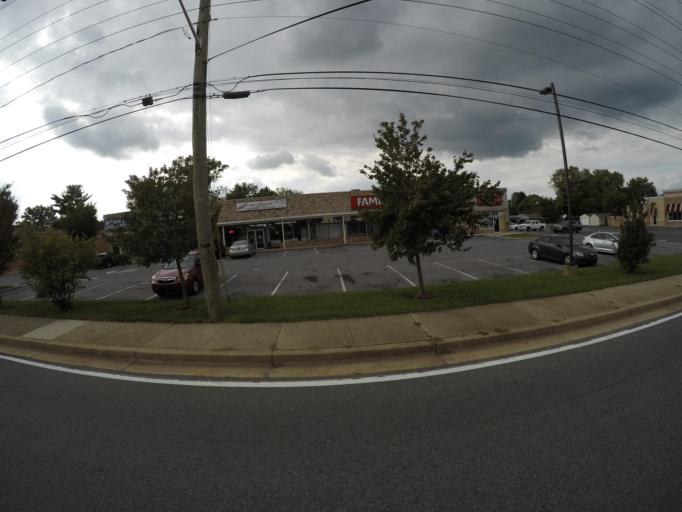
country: US
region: Delaware
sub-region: New Castle County
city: Brookside
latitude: 39.6637
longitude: -75.7269
